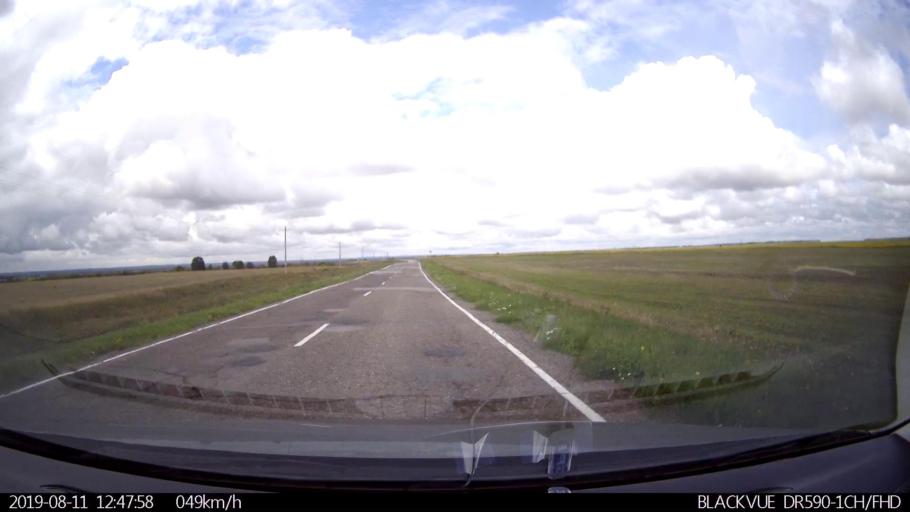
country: RU
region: Ulyanovsk
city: Ignatovka
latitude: 53.8718
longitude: 47.7037
